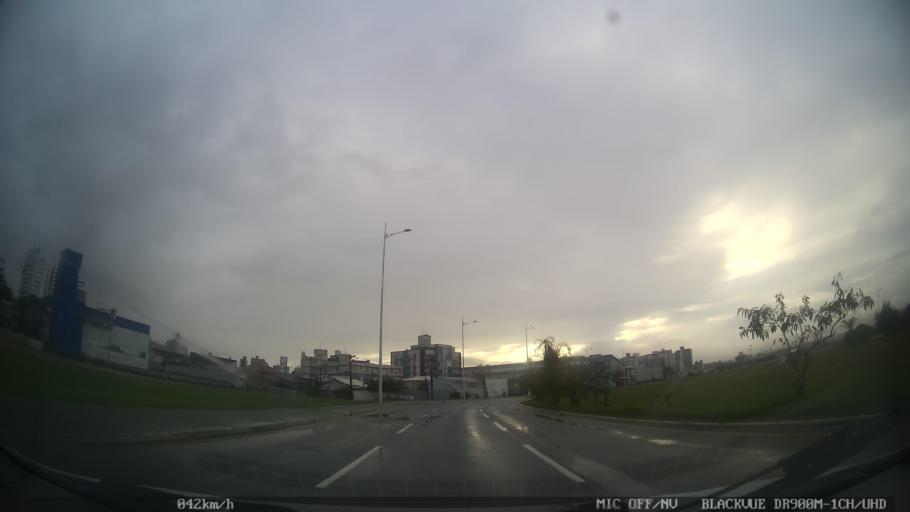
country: BR
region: Santa Catarina
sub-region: Sao Jose
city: Campinas
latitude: -27.6031
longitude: -48.6177
